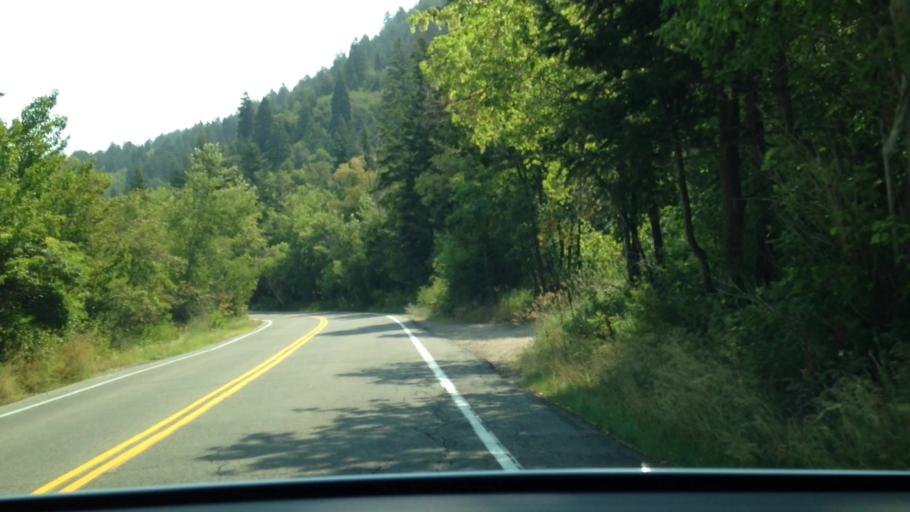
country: US
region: Utah
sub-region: Salt Lake County
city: Mount Olympus
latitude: 40.6978
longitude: -111.7295
